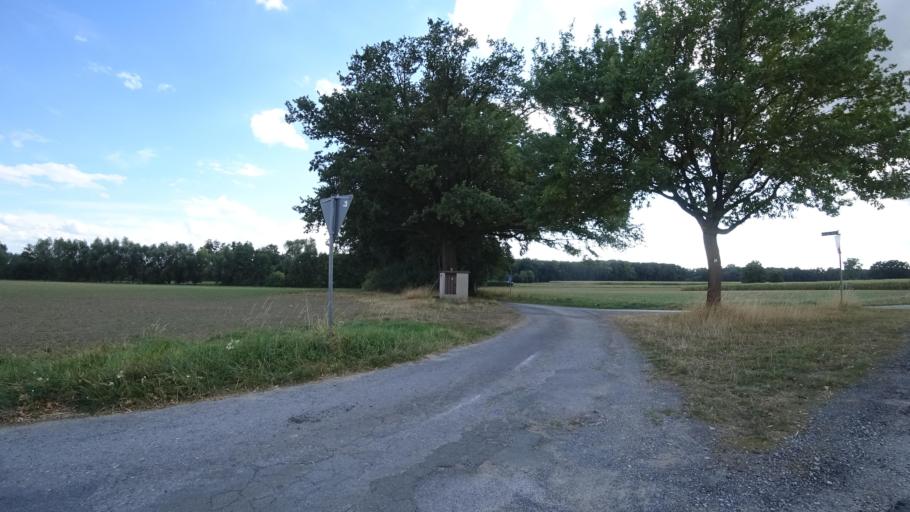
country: DE
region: North Rhine-Westphalia
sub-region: Regierungsbezirk Detmold
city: Rheda-Wiedenbruck
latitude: 51.8350
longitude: 8.2740
